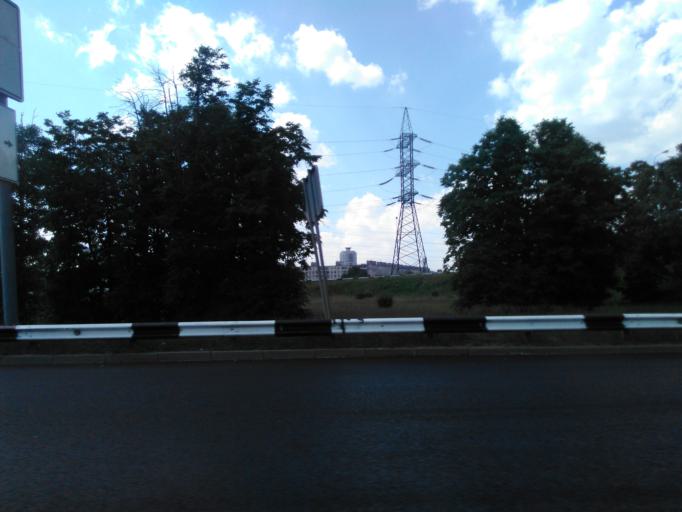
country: RU
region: Moscow
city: Veshnyaki
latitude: 55.7182
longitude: 37.8388
